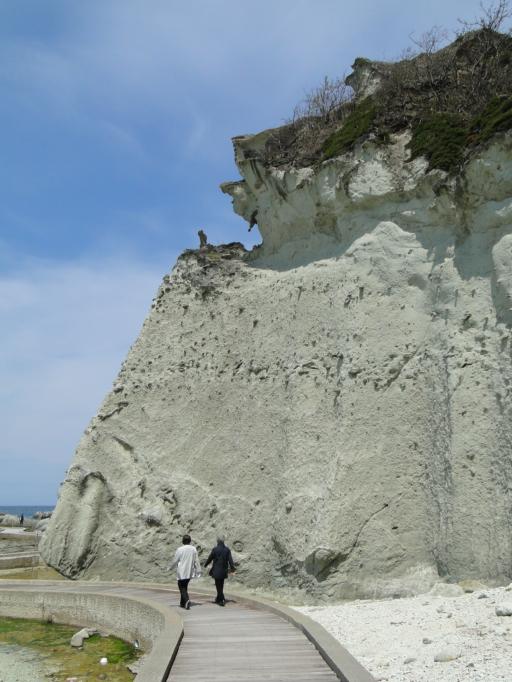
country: JP
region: Aomori
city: Mutsu
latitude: 41.3109
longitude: 140.8048
